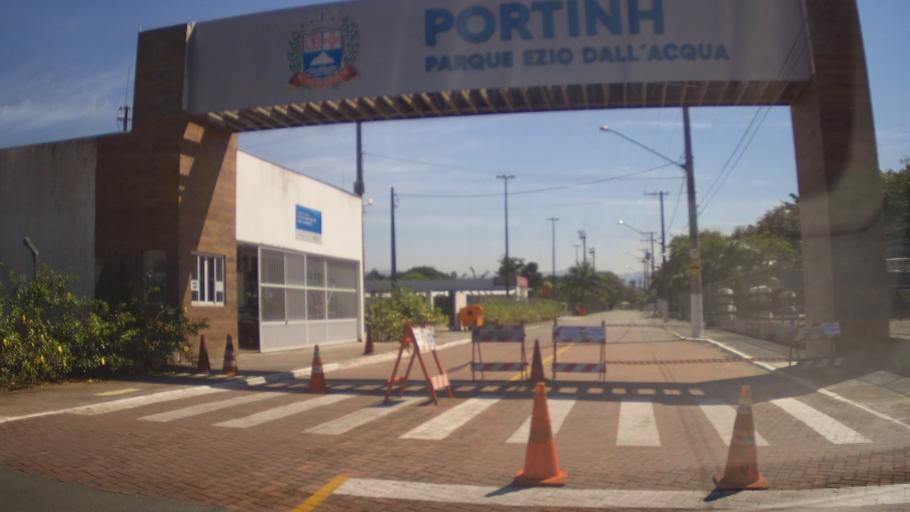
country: BR
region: Sao Paulo
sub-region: Praia Grande
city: Praia Grande
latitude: -23.9907
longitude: -46.4053
